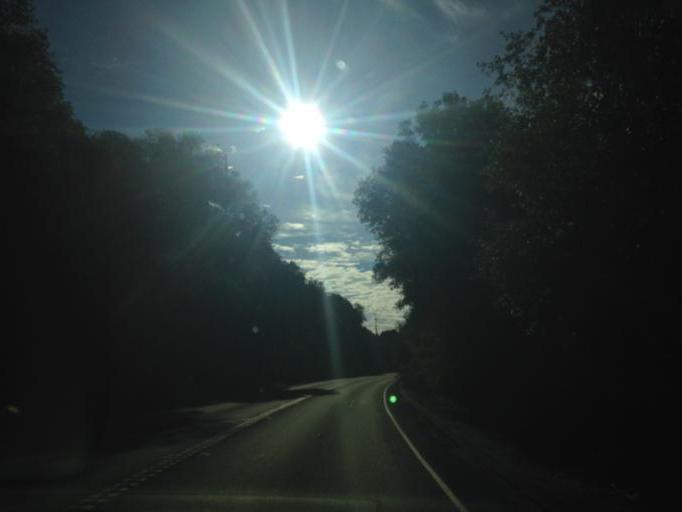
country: US
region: California
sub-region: Riverside County
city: Aguanga
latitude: 33.2498
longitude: -116.7873
